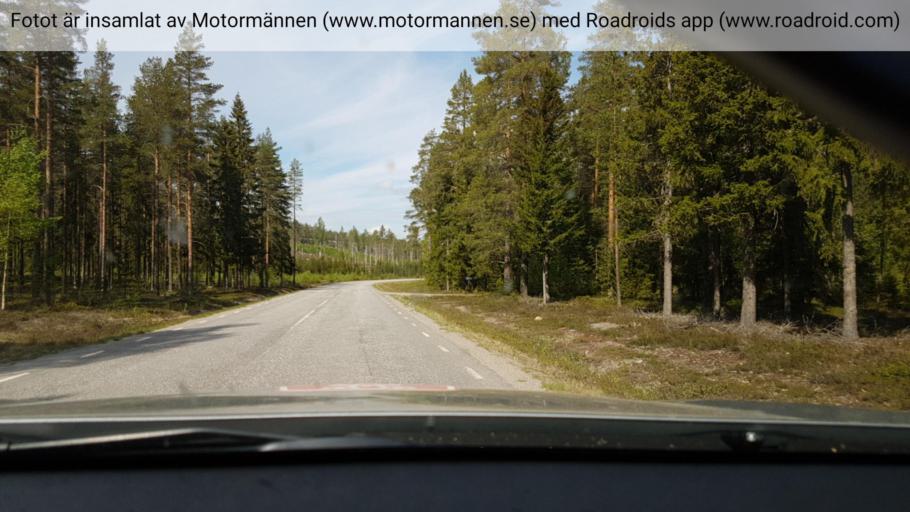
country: SE
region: Vaesterbotten
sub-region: Umea Kommun
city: Roback
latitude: 63.8436
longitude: 20.0915
